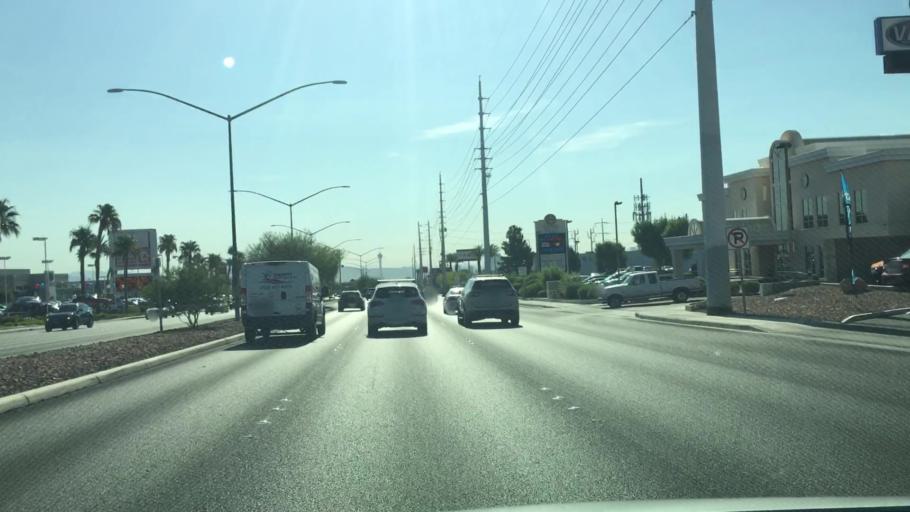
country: US
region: Nevada
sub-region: Clark County
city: Spring Valley
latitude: 36.1439
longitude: -115.2494
